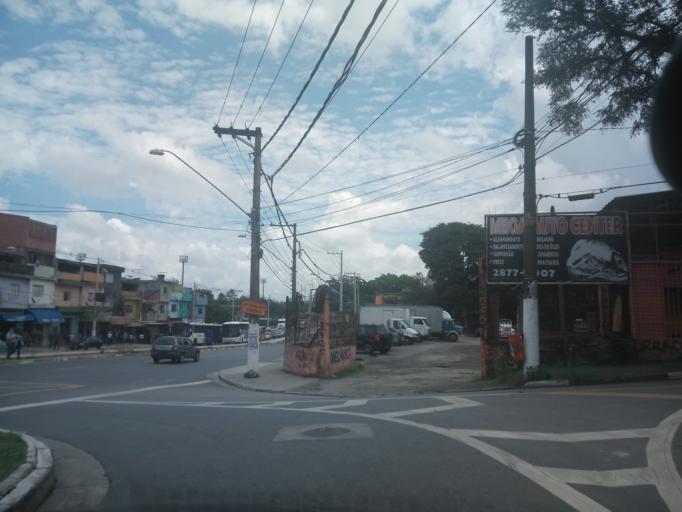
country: BR
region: Sao Paulo
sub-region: Sao Bernardo Do Campo
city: Sao Bernardo do Campo
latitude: -23.7353
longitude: -46.5816
